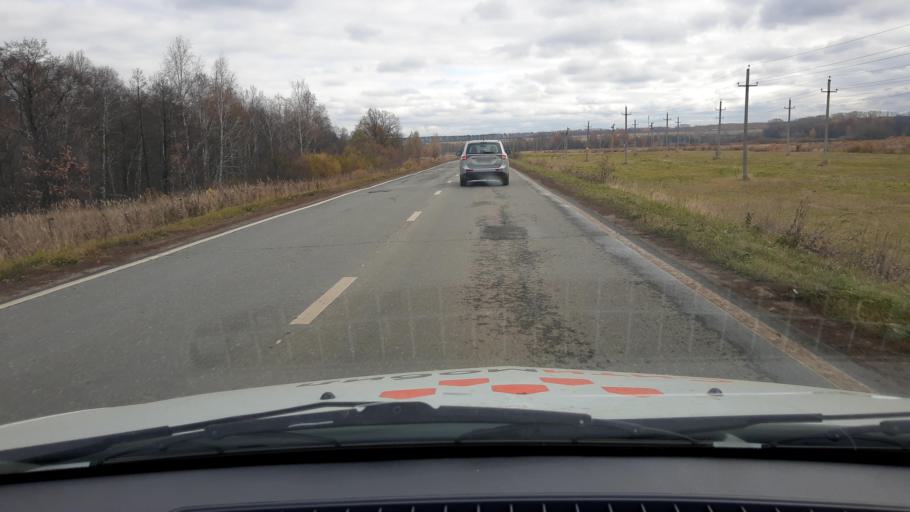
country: RU
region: Bashkortostan
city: Iglino
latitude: 54.7427
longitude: 56.2209
